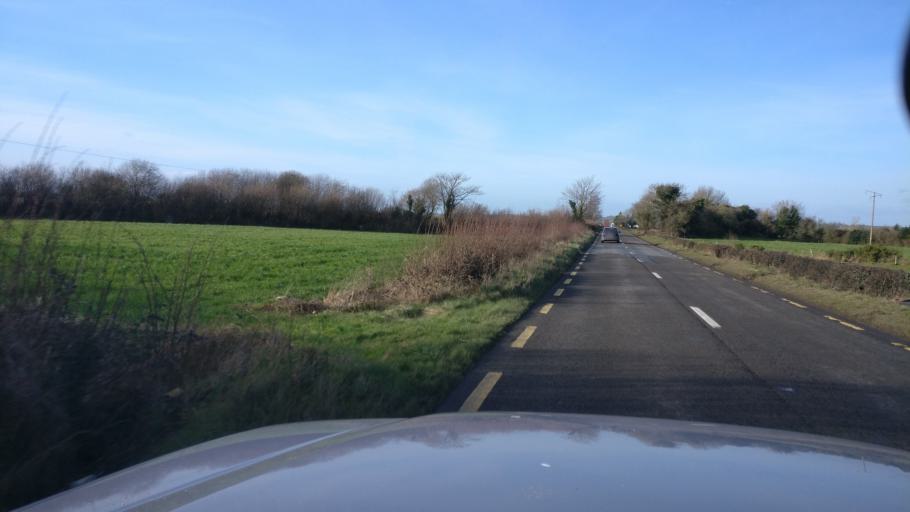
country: IE
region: Leinster
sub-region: Laois
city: Mountmellick
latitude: 53.1733
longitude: -7.3843
